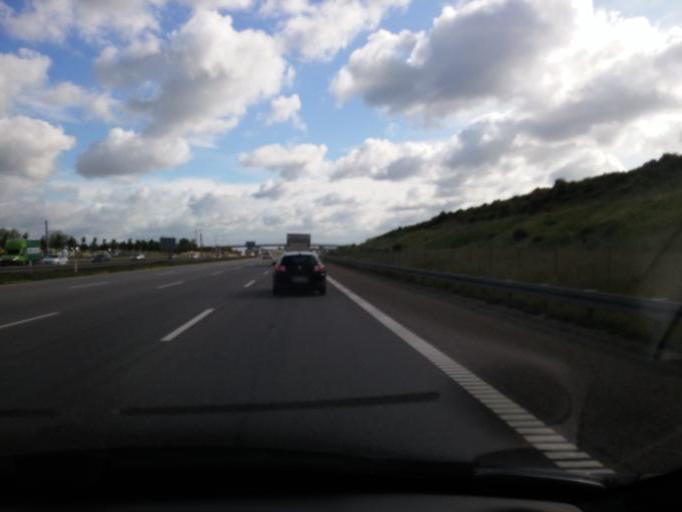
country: DK
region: Zealand
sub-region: Greve Kommune
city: Greve
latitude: 55.5873
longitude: 12.2665
